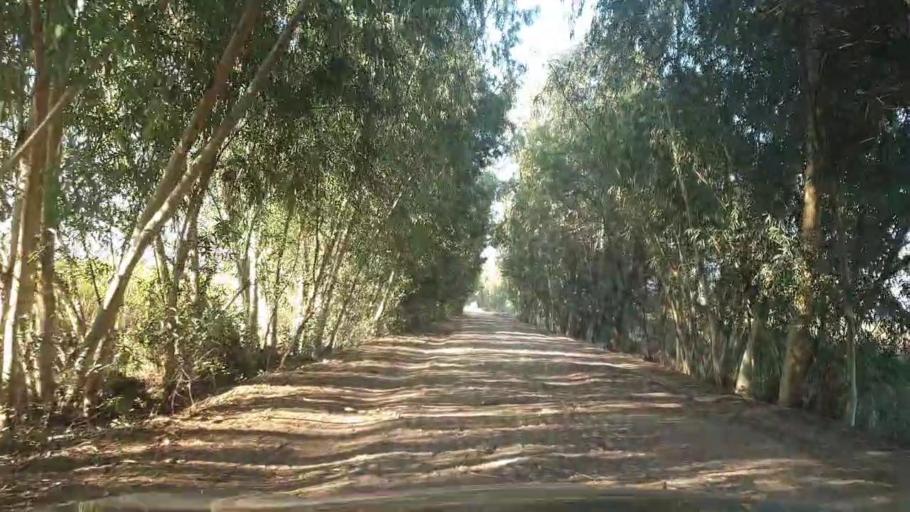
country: PK
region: Sindh
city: Khairpur
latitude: 28.1431
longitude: 69.6110
